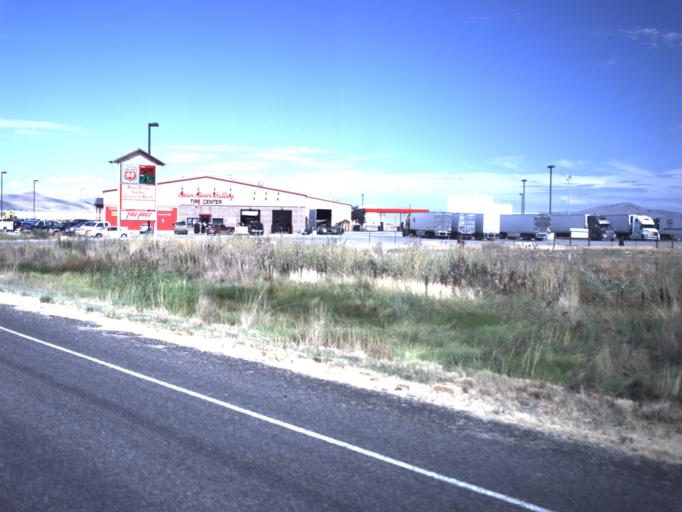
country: US
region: Utah
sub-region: Box Elder County
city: Honeyville
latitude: 41.5545
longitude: -112.1267
